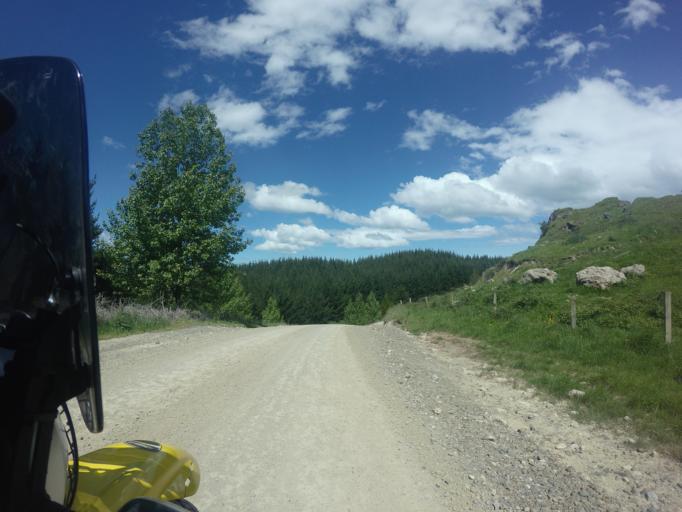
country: NZ
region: Hawke's Bay
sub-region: Wairoa District
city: Wairoa
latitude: -38.9877
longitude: 177.7252
